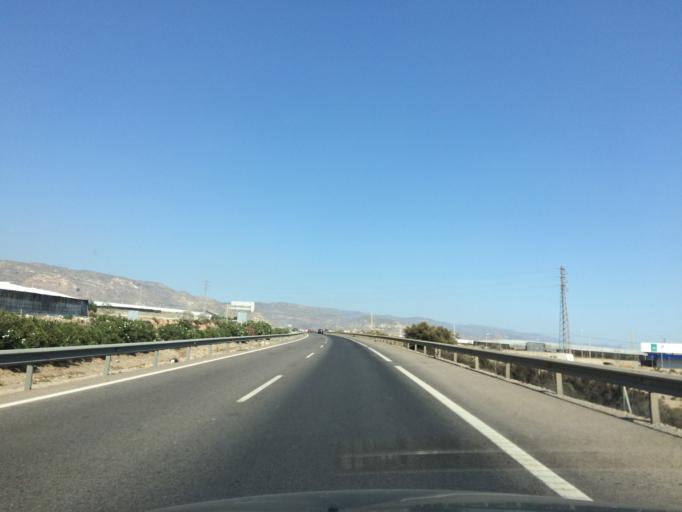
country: ES
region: Andalusia
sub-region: Provincia de Almeria
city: Vicar
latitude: 36.7995
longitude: -2.6800
